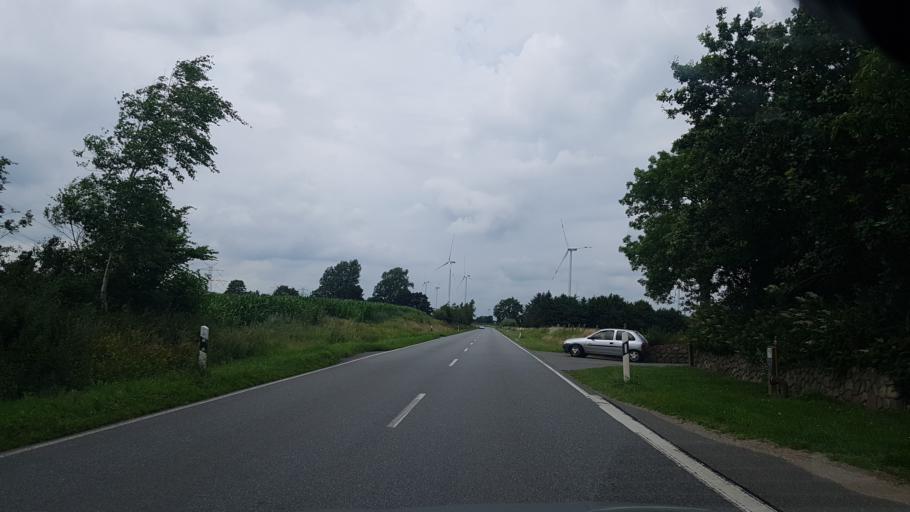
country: DE
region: Schleswig-Holstein
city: Jardelund
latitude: 54.8379
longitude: 9.2121
